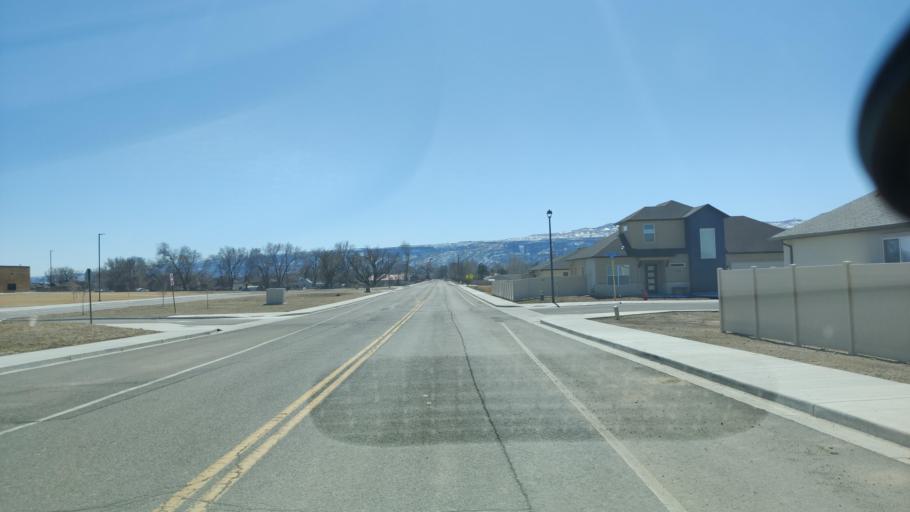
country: US
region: Colorado
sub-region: Mesa County
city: Fruita
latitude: 39.1716
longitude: -108.7105
